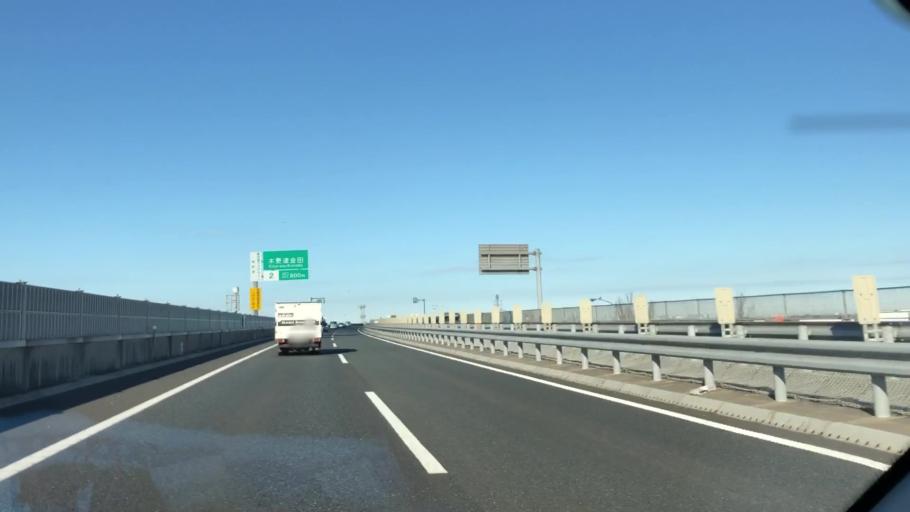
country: JP
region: Chiba
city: Kisarazu
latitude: 35.4219
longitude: 139.9361
